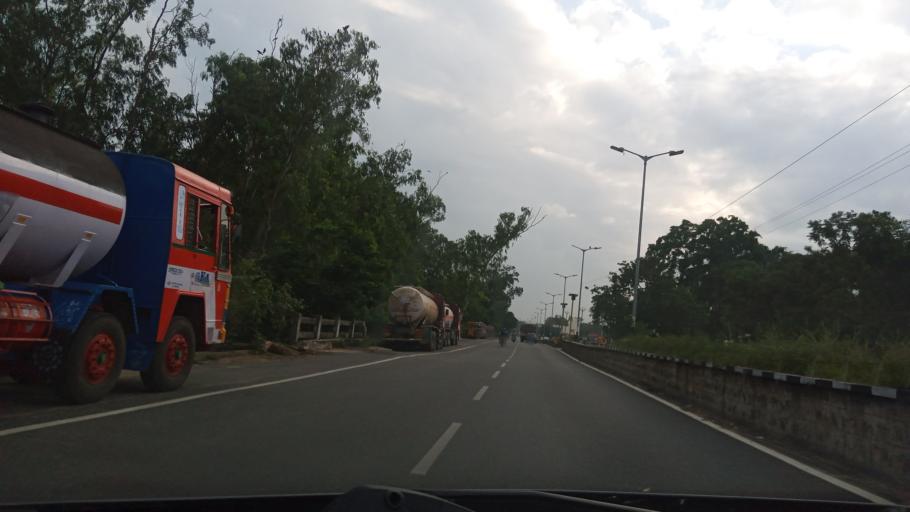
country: IN
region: Tamil Nadu
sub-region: Villupuram
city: Auroville
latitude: 12.0274
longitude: 79.8625
